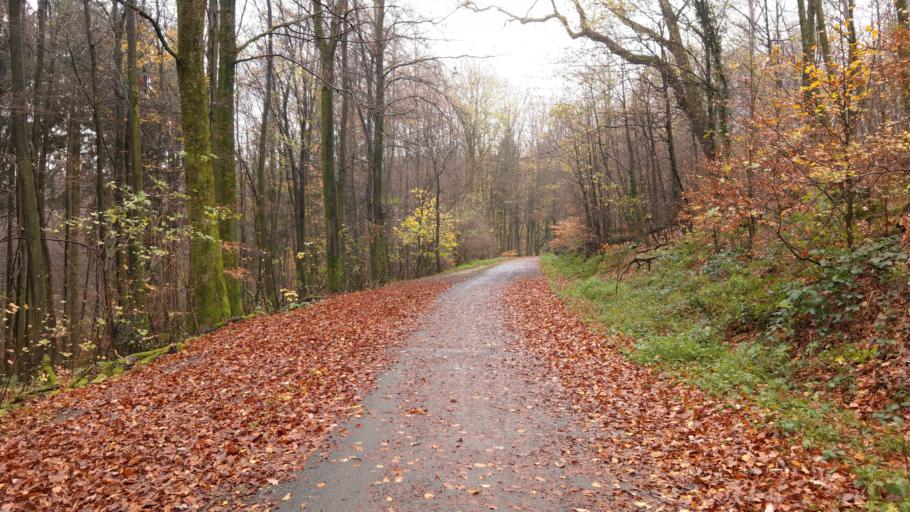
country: DE
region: North Rhine-Westphalia
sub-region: Regierungsbezirk Koln
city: Aachen
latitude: 50.7376
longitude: 6.0712
